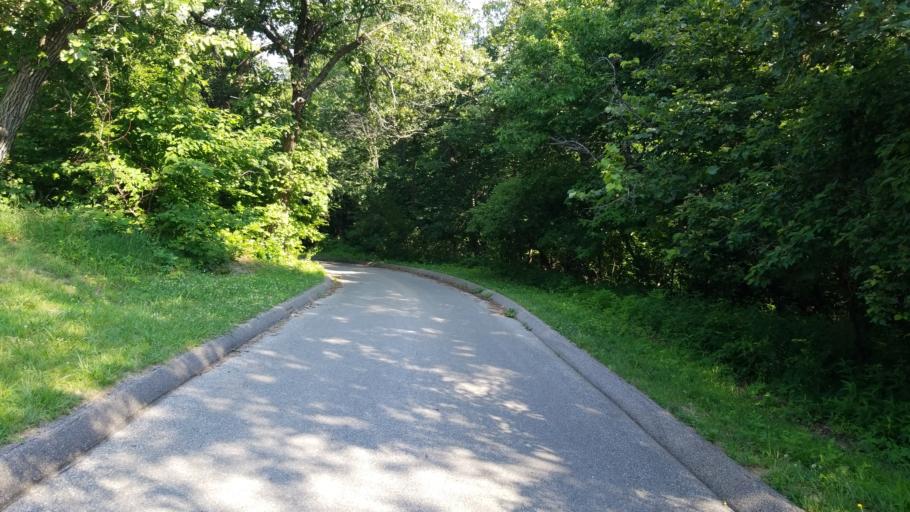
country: US
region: Nebraska
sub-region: Cass County
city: Louisville
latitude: 41.0210
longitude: -96.2449
